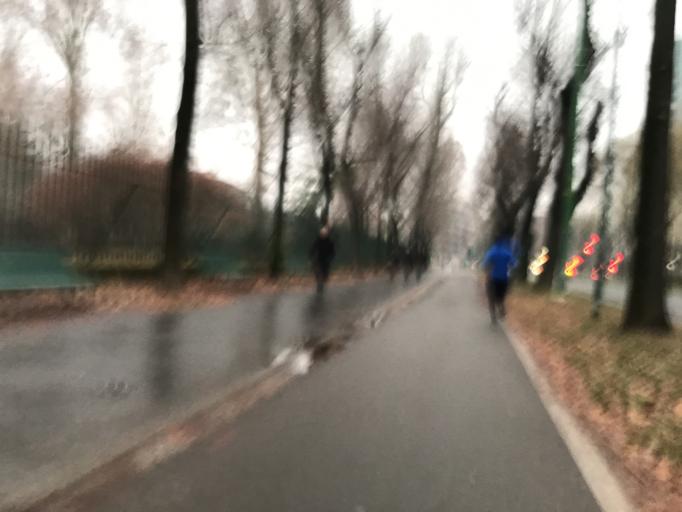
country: IT
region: Lombardy
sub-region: Citta metropolitana di Milano
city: Milano
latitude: 45.4760
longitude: 9.1812
